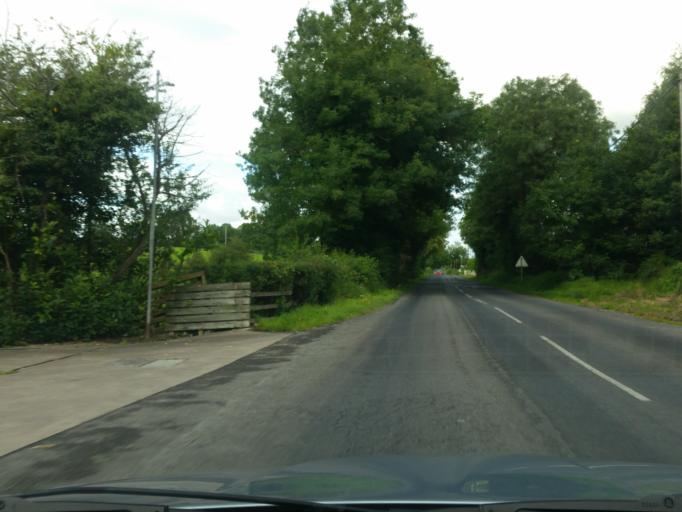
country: IE
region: Ulster
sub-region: An Cabhan
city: Belturbet
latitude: 54.1449
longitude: -7.3547
